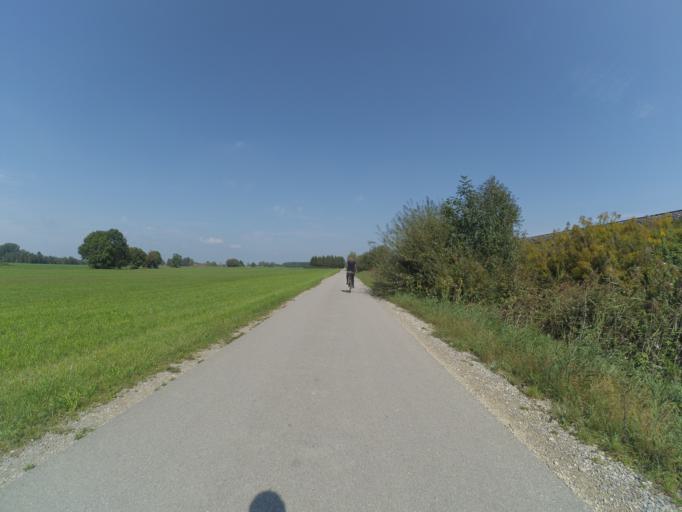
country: DE
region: Bavaria
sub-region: Swabia
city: Lamerdingen
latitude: 48.0713
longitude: 10.7288
